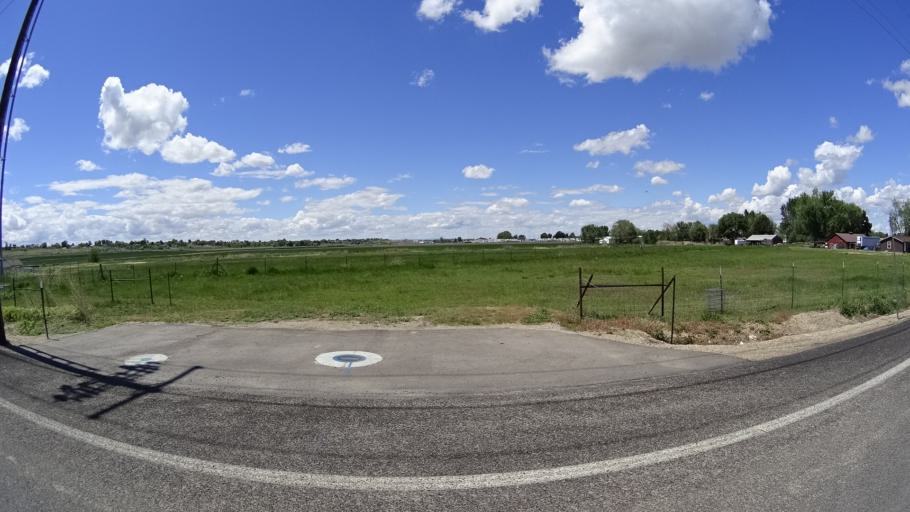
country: US
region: Idaho
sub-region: Ada County
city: Meridian
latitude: 43.6032
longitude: -116.4537
